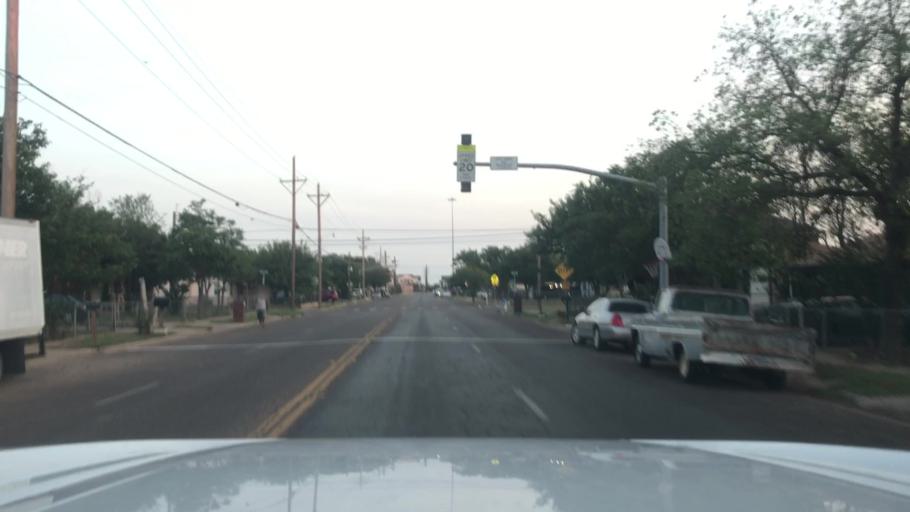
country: US
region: Texas
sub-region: Lubbock County
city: Lubbock
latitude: 33.5968
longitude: -101.8619
